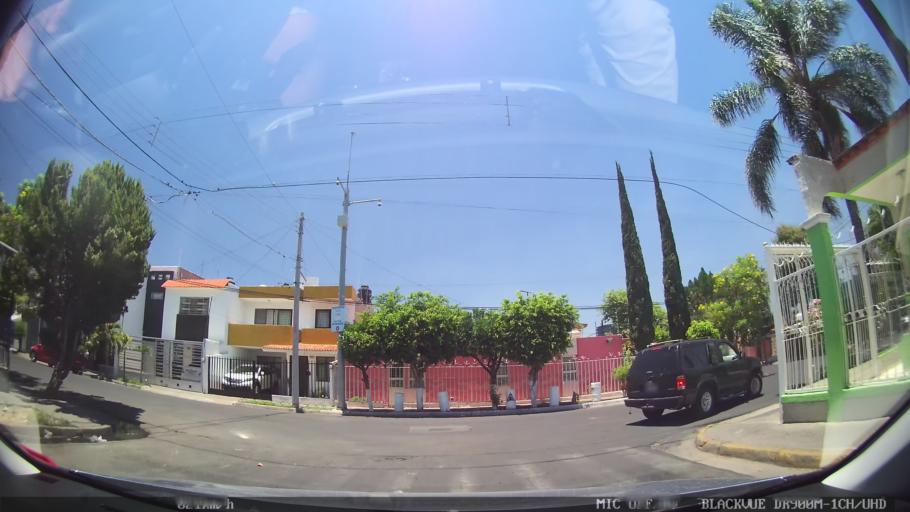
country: MX
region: Jalisco
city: Tlaquepaque
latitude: 20.6775
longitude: -103.2837
